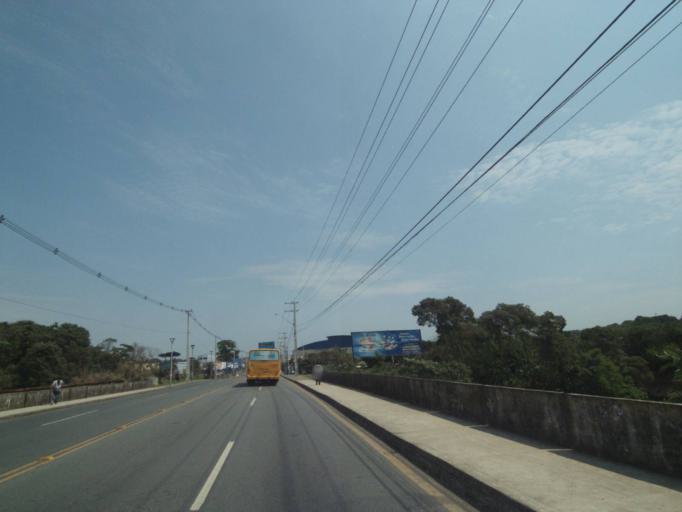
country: BR
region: Parana
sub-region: Curitiba
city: Curitiba
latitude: -25.4782
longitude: -49.3309
